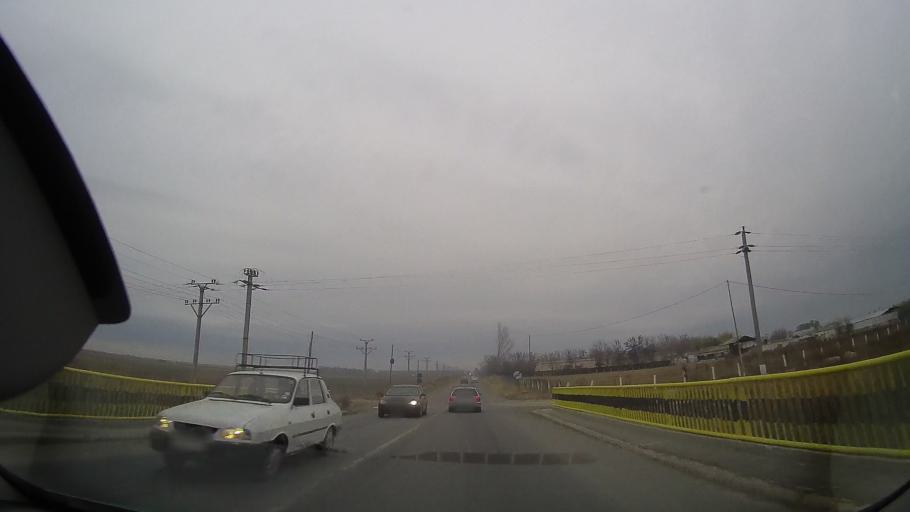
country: RO
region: Ialomita
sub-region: Oras Amara
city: Amara
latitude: 44.5852
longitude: 27.3338
